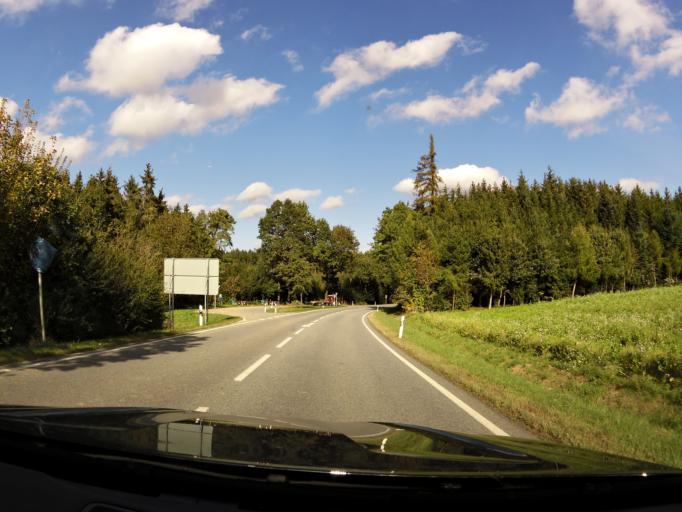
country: DE
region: Bavaria
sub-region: Lower Bavaria
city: Vilsheim
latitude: 48.4309
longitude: 12.1392
